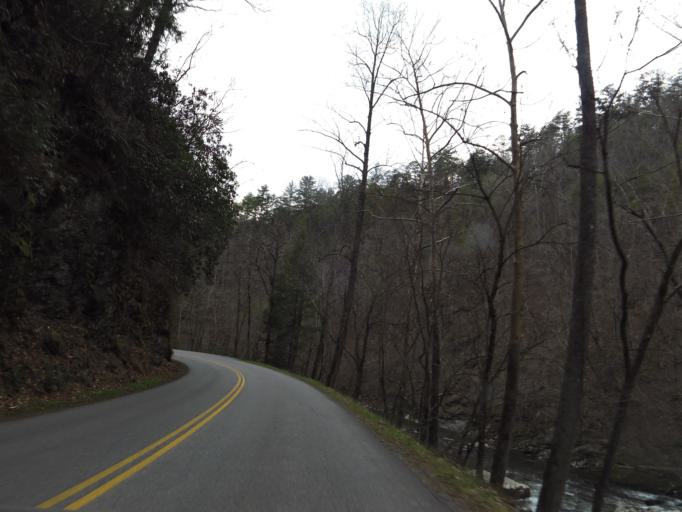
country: US
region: Tennessee
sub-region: Sevier County
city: Pigeon Forge
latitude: 35.6626
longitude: -83.7058
